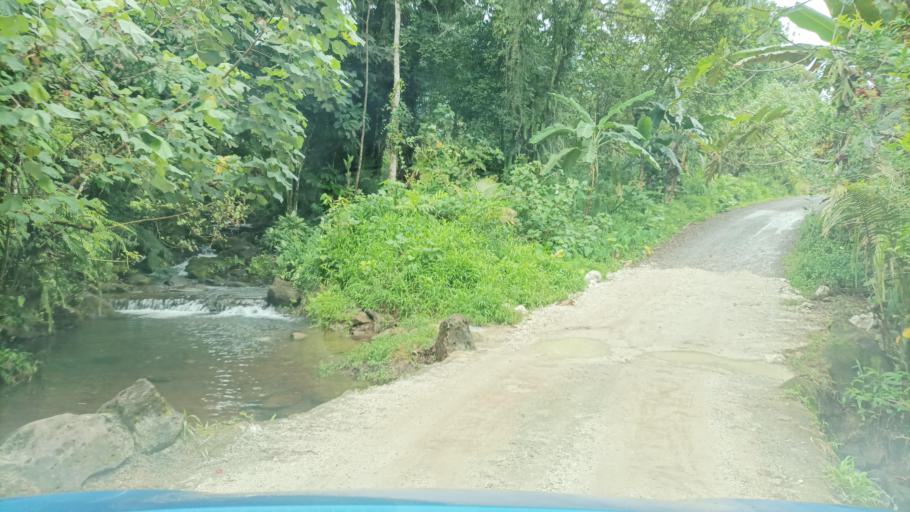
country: FM
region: Pohnpei
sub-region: Sokehs Municipality
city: Palikir - National Government Center
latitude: 6.8500
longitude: 158.1797
